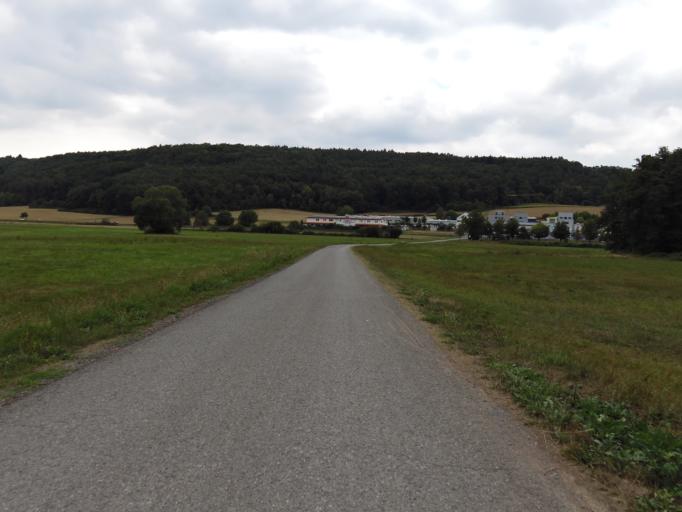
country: DE
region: Bavaria
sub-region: Regierungsbezirk Unterfranken
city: Momlingen
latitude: 49.8472
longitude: 9.0764
